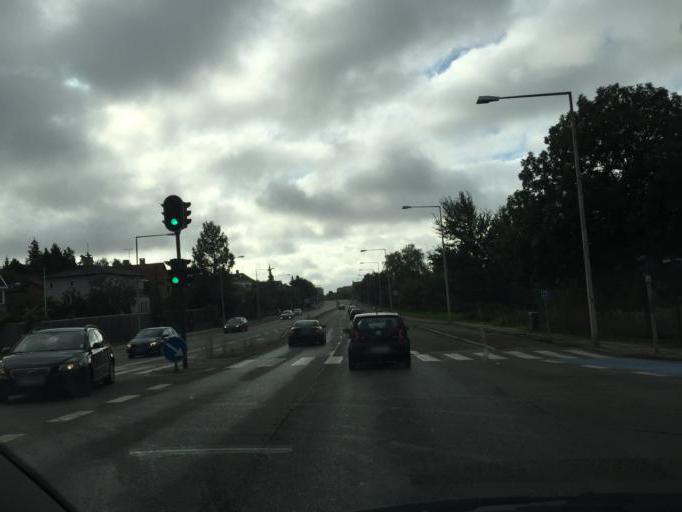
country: DK
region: Capital Region
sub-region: Kobenhavn
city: Vanlose
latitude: 55.7128
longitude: 12.5045
